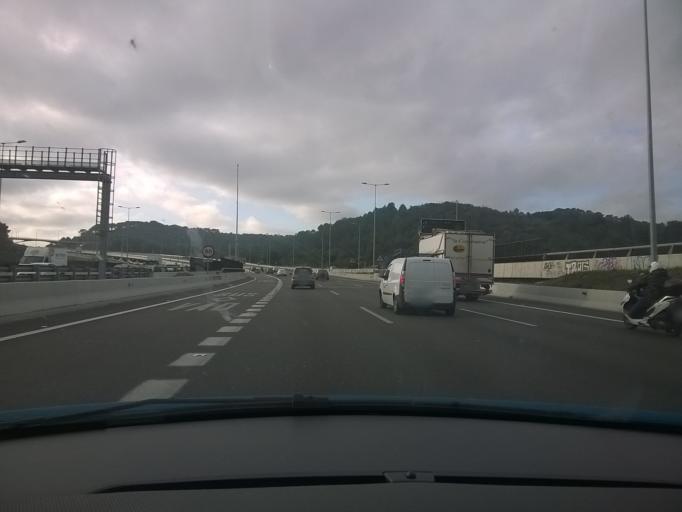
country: ES
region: Catalonia
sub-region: Provincia de Barcelona
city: Ripollet
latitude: 41.4836
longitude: 2.1600
